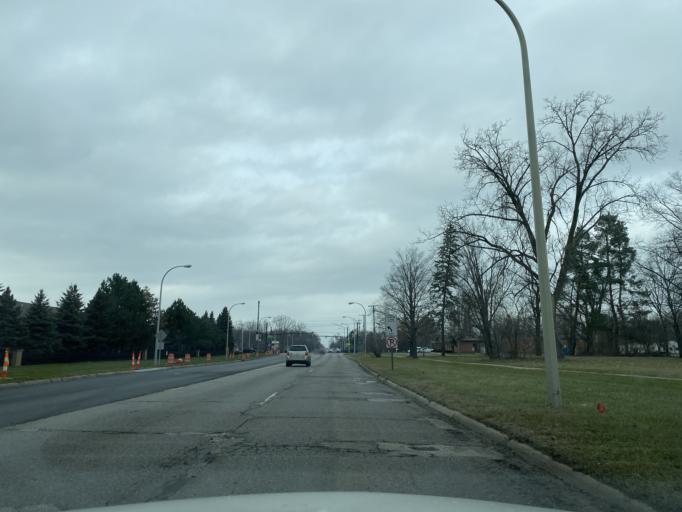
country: US
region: Michigan
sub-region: Wayne County
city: Taylor
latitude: 42.2244
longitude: -83.2882
